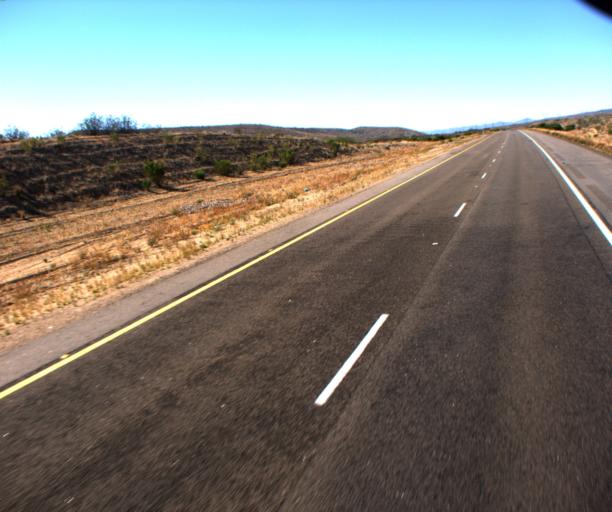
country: US
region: Arizona
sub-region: Mohave County
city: Kingman
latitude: 34.9839
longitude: -113.6681
